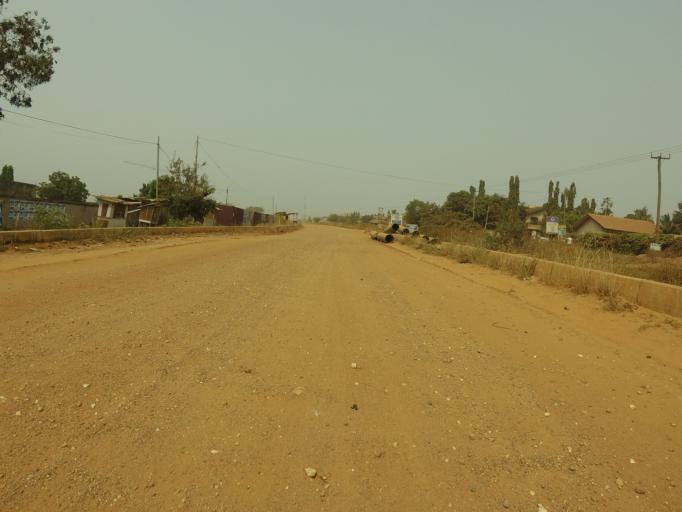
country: GH
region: Greater Accra
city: Teshi Old Town
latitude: 5.6313
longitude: -0.1243
